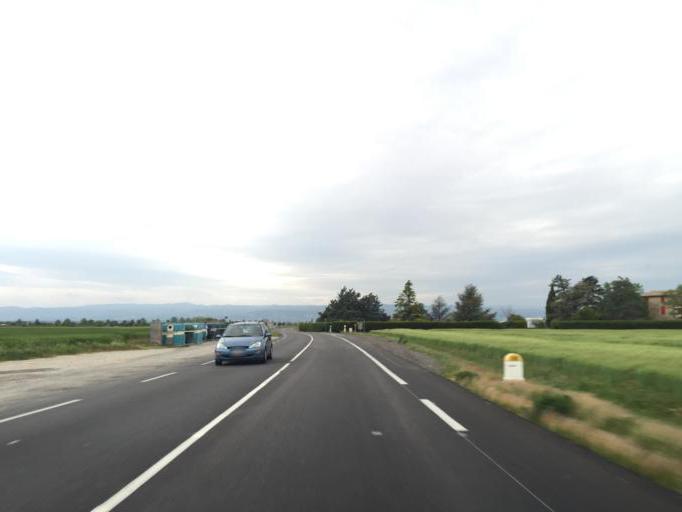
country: FR
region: Rhone-Alpes
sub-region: Departement de la Drome
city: Chabeuil
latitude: 44.9123
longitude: 5.0283
